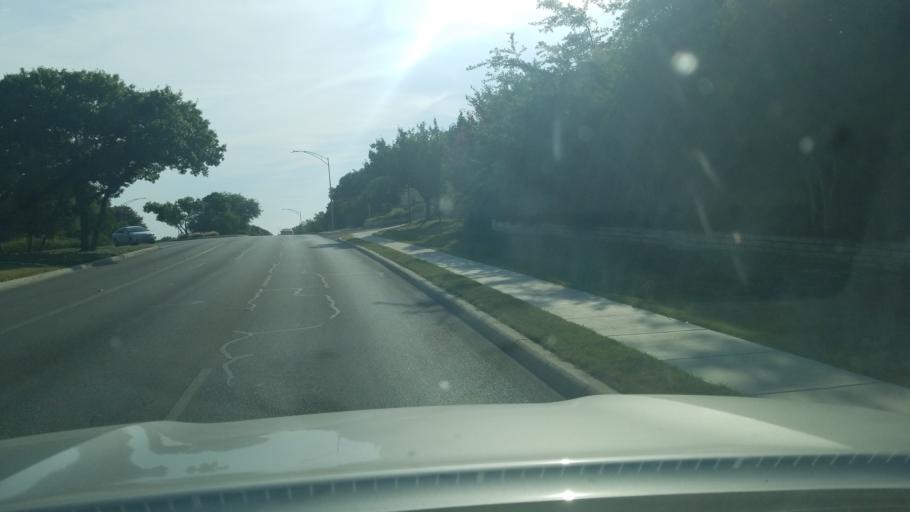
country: US
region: Texas
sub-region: Bexar County
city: Hollywood Park
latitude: 29.6265
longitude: -98.5006
